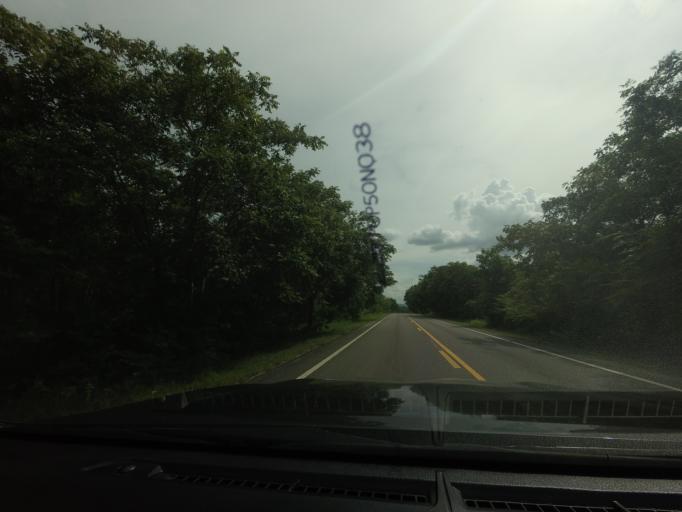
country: TH
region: Kanchanaburi
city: Kanchanaburi
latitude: 14.1436
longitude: 99.4163
